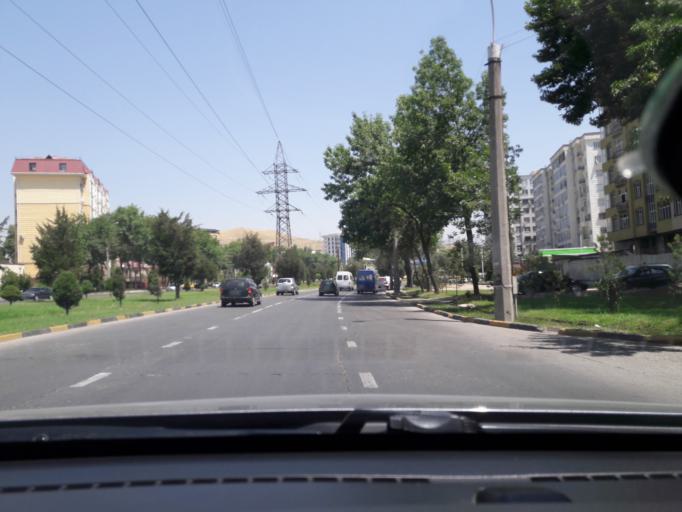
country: TJ
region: Dushanbe
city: Dushanbe
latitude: 38.5888
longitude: 68.7414
